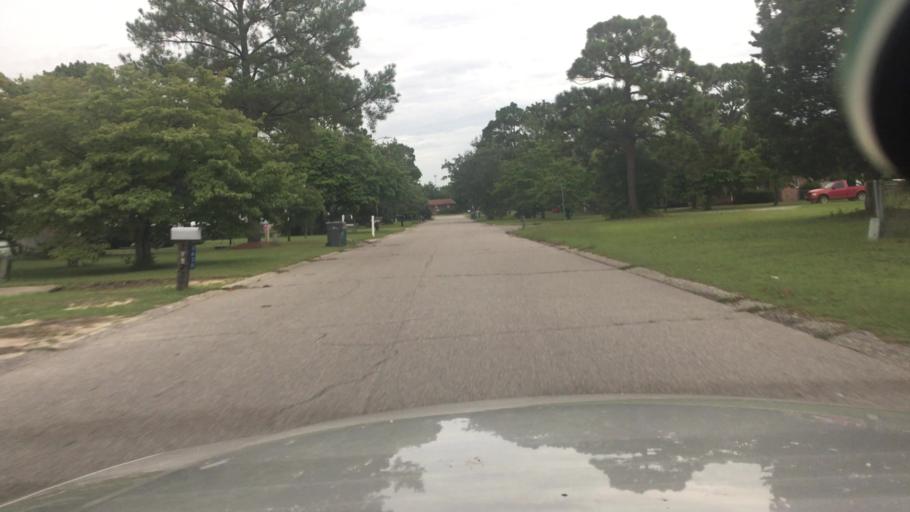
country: US
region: North Carolina
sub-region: Cumberland County
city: Hope Mills
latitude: 34.9709
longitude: -78.9718
